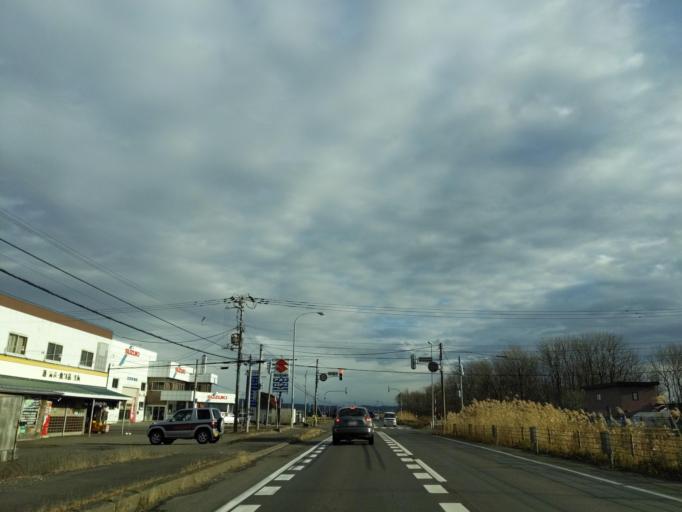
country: JP
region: Hokkaido
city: Kitahiroshima
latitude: 42.9628
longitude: 141.6830
